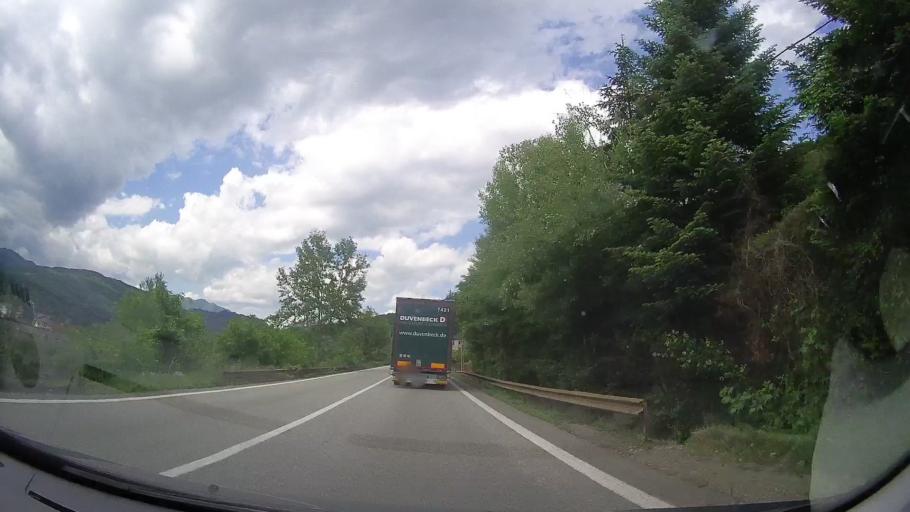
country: RO
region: Valcea
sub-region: Oras Calimanesti
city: Jiblea Veche
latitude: 45.2566
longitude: 24.3368
